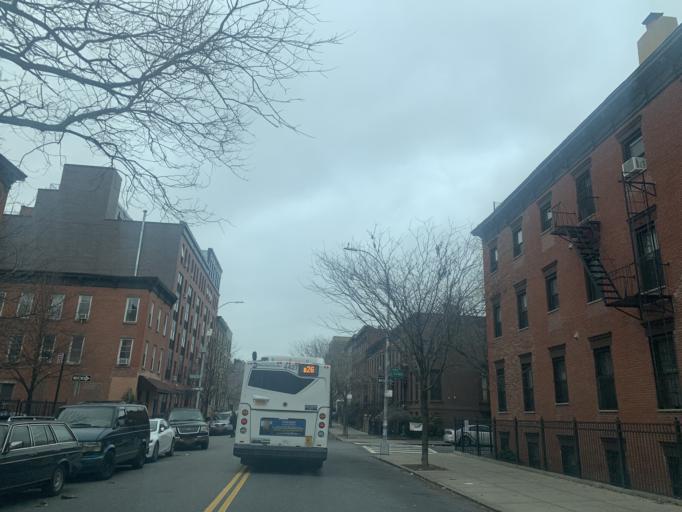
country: US
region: New York
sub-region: Kings County
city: Brooklyn
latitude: 40.6830
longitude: -73.9593
